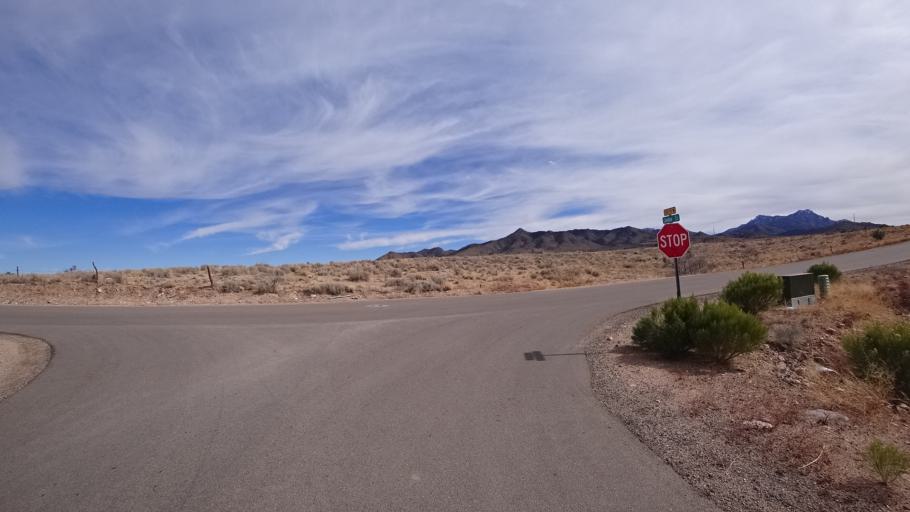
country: US
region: Arizona
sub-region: Mohave County
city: Kingman
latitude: 35.1861
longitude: -113.9764
